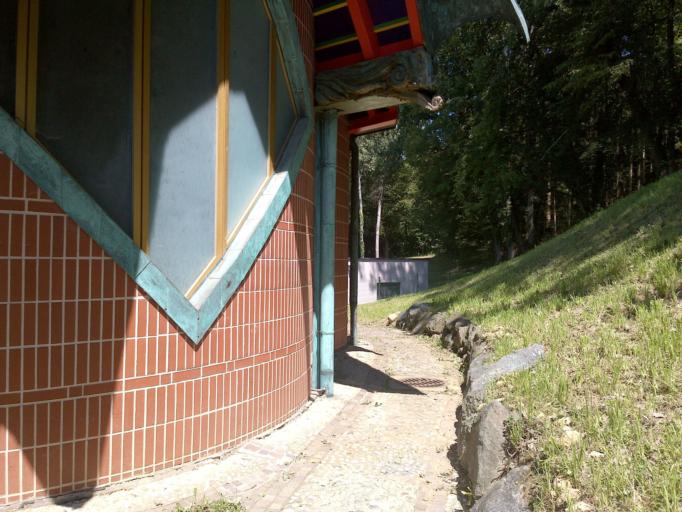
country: AT
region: Styria
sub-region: Politischer Bezirk Graz-Umgebung
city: Thal
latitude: 47.0762
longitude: 15.3620
